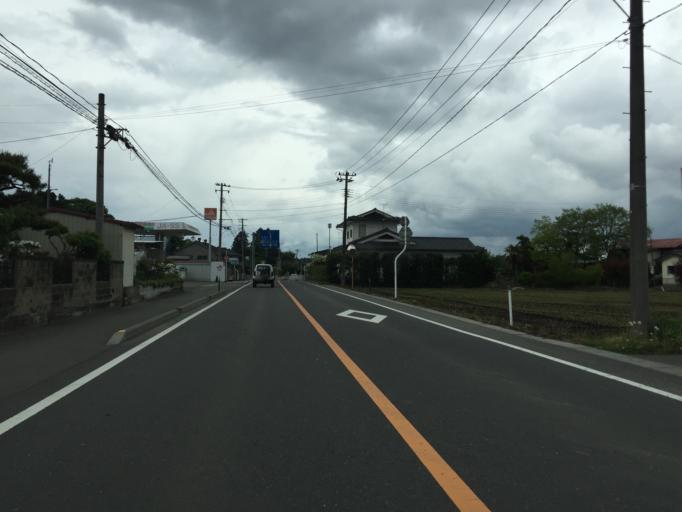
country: JP
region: Fukushima
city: Sukagawa
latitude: 37.1950
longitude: 140.3723
